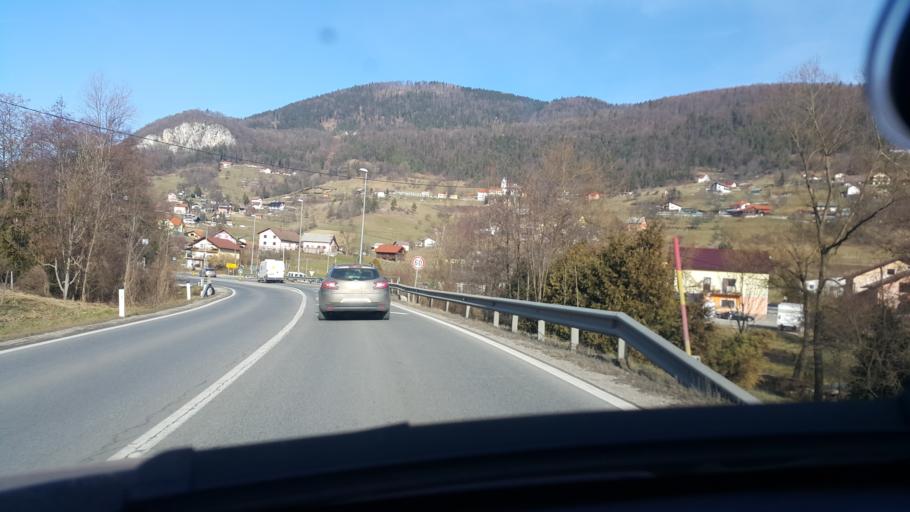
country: SI
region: Dobrna
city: Dobrna
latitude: 46.3401
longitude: 15.1728
